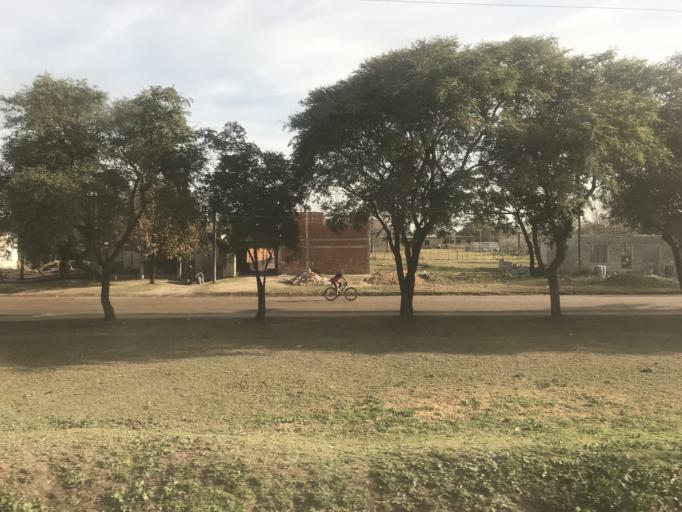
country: AR
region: Cordoba
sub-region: Departamento de Rio Segundo
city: Rio Segundo
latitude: -31.6581
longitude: -63.9066
